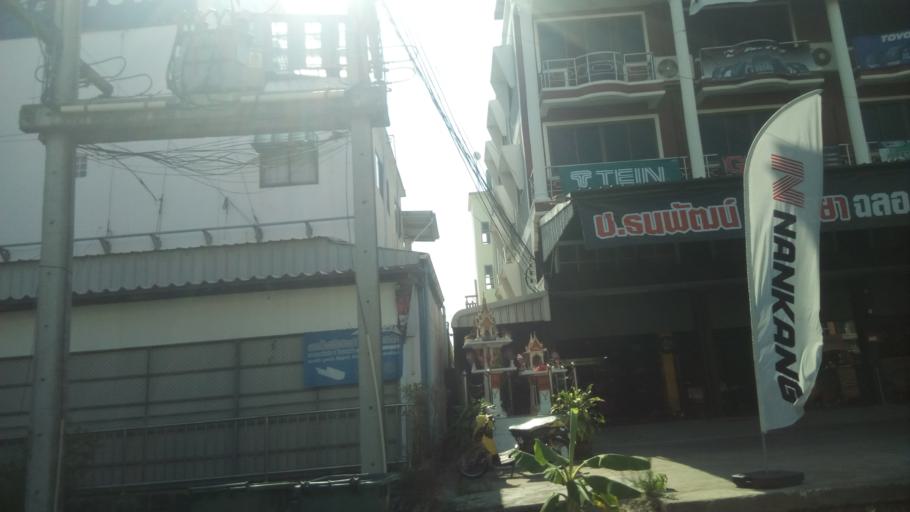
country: TH
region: Nakhon Pathom
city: Salaya
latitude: 13.8029
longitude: 100.3037
